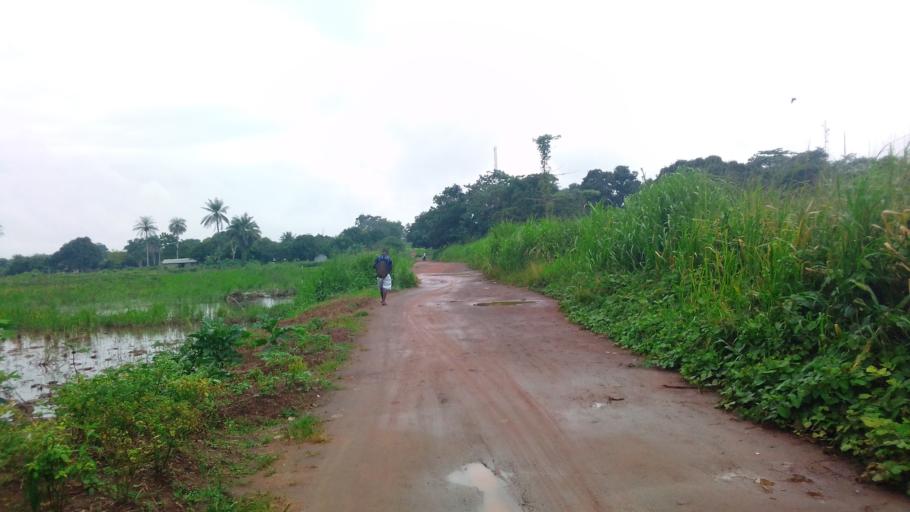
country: SL
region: Northern Province
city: Lunsar
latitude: 8.6873
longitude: -12.5241
